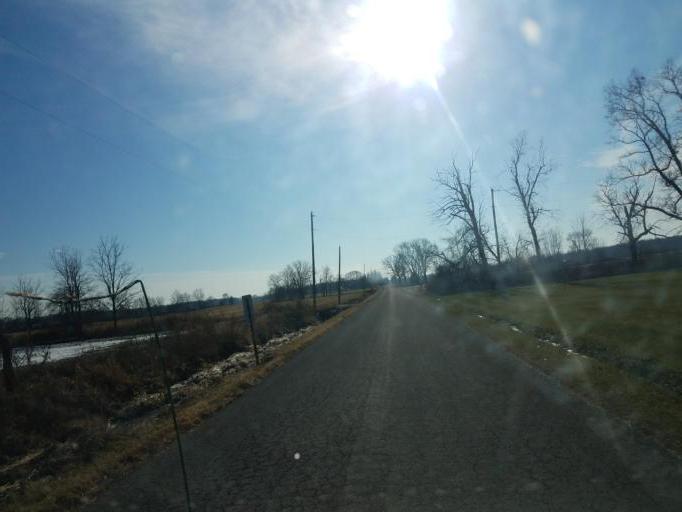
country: US
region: Ohio
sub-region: Morrow County
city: Cardington
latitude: 40.4568
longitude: -82.8713
